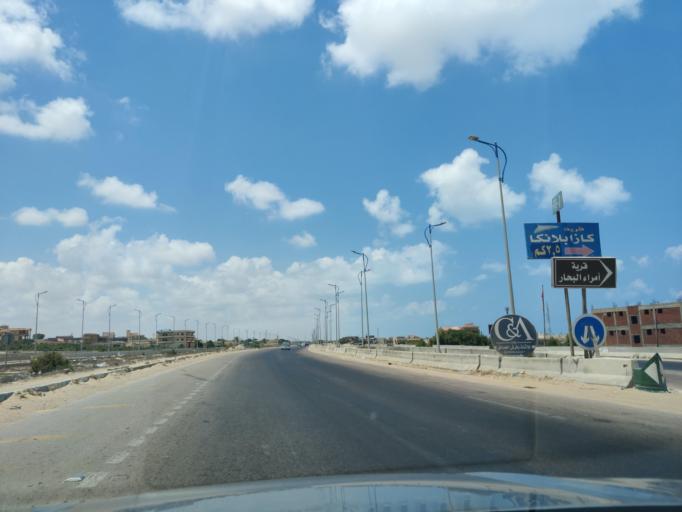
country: EG
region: Alexandria
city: Alexandria
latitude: 30.9634
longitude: 29.5490
